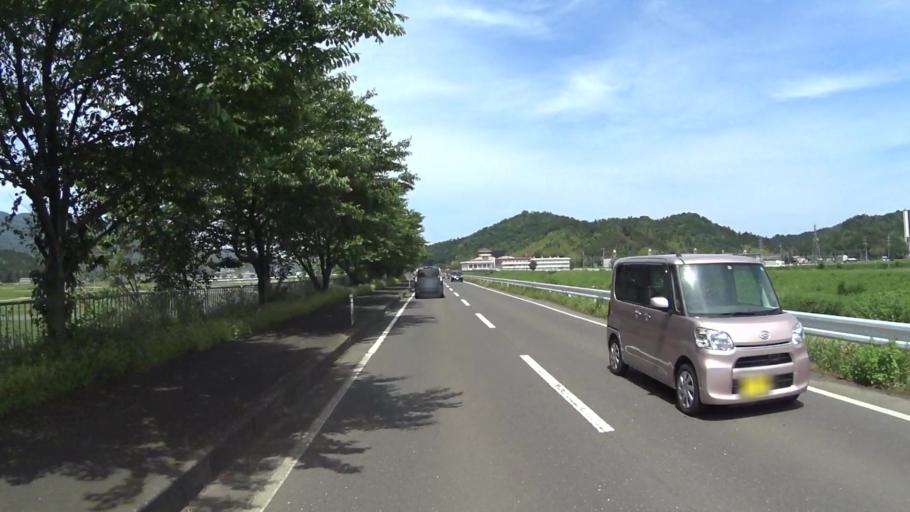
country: JP
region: Fukui
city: Obama
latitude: 35.4680
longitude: 135.6180
